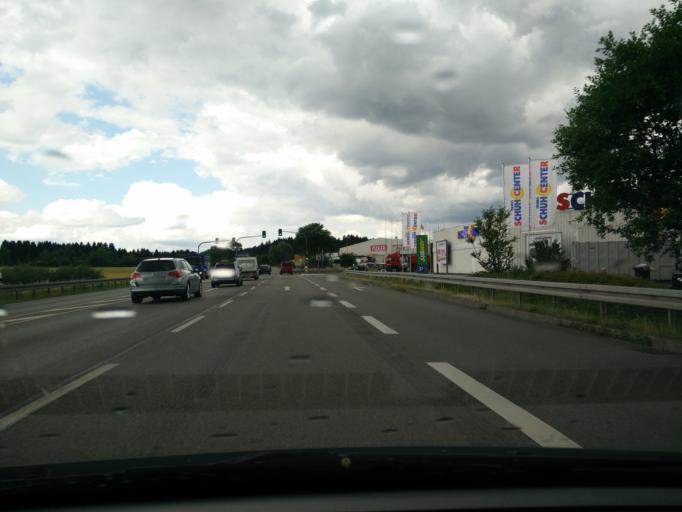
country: DE
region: Baden-Wuerttemberg
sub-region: Freiburg Region
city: Bad Durrheim
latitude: 48.0335
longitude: 8.5281
